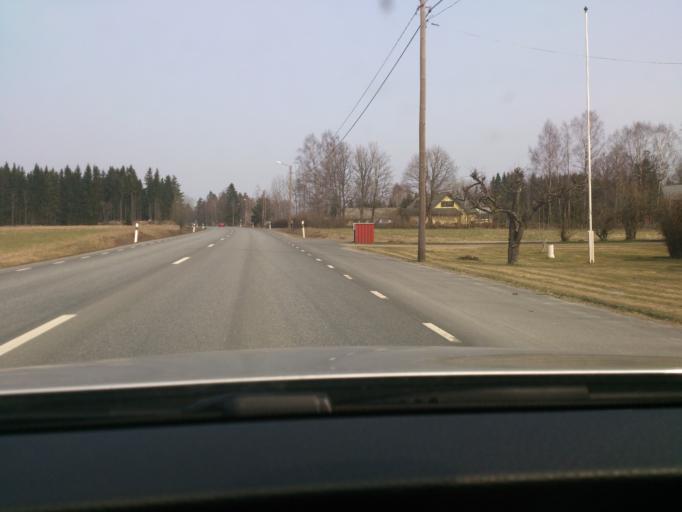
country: SE
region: Kronoberg
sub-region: Alvesta Kommun
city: Moheda
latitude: 56.9789
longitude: 14.5681
